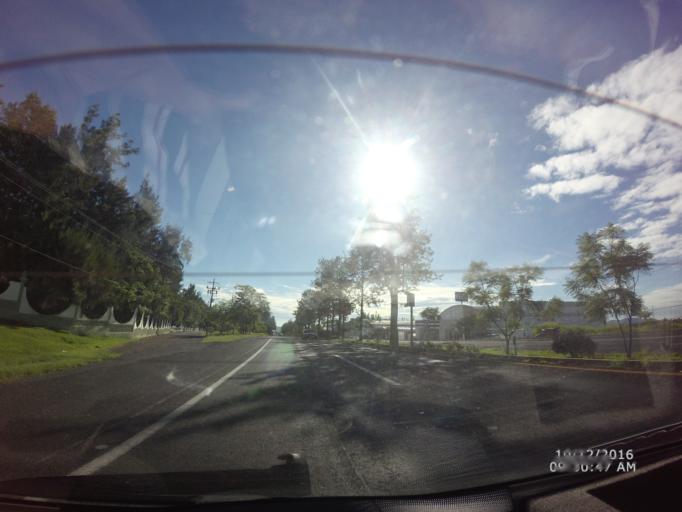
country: TR
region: Sivas
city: Sivas
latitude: 39.6813
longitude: 37.0499
